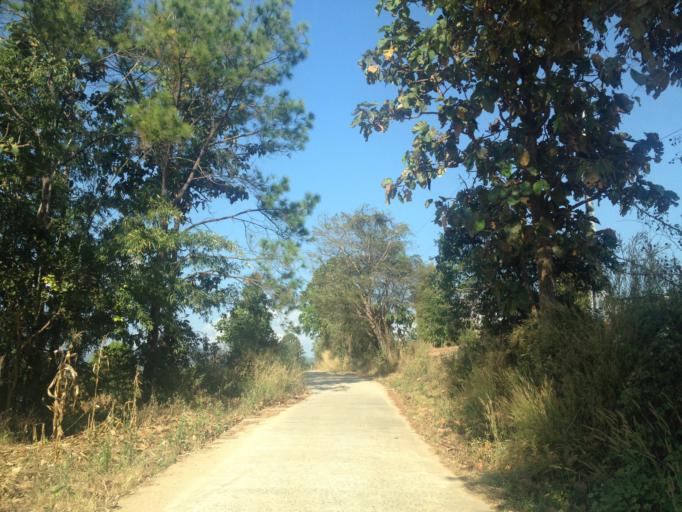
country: TH
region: Mae Hong Son
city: Ban Huai I Huak
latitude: 18.1079
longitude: 98.2176
